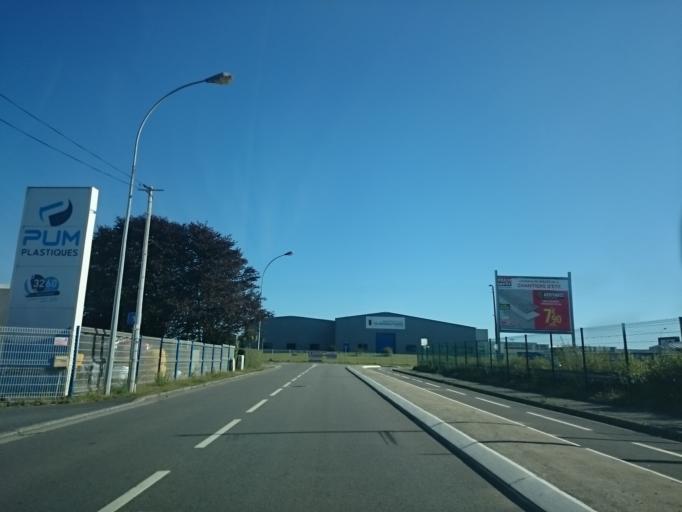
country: FR
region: Brittany
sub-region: Departement du Finistere
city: Gouesnou
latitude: 48.4236
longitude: -4.4603
